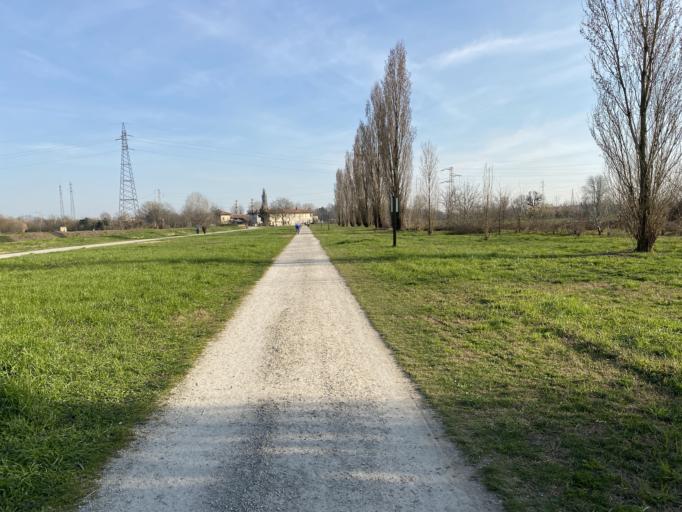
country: IT
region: Lombardy
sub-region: Citta metropolitana di Milano
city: Chiaravalle
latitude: 45.4212
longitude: 9.2306
